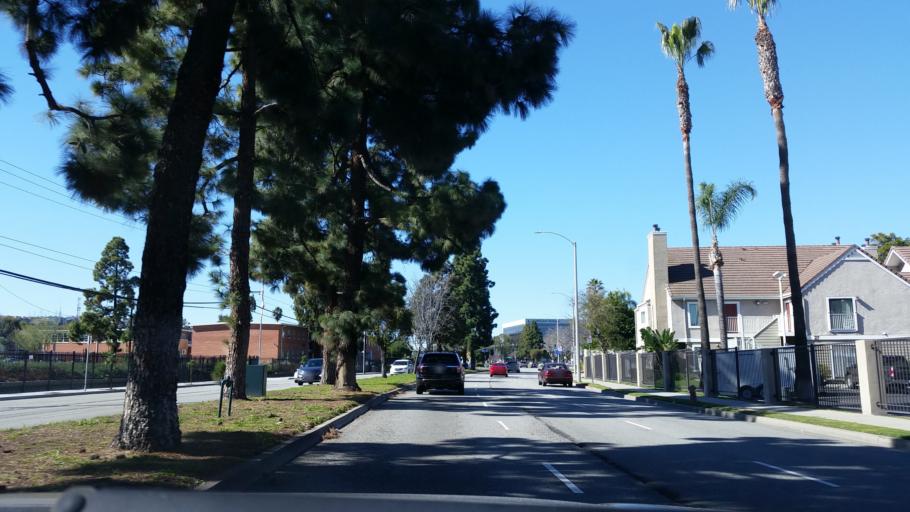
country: US
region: California
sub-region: Los Angeles County
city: Signal Hill
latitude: 33.8035
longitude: -118.1453
